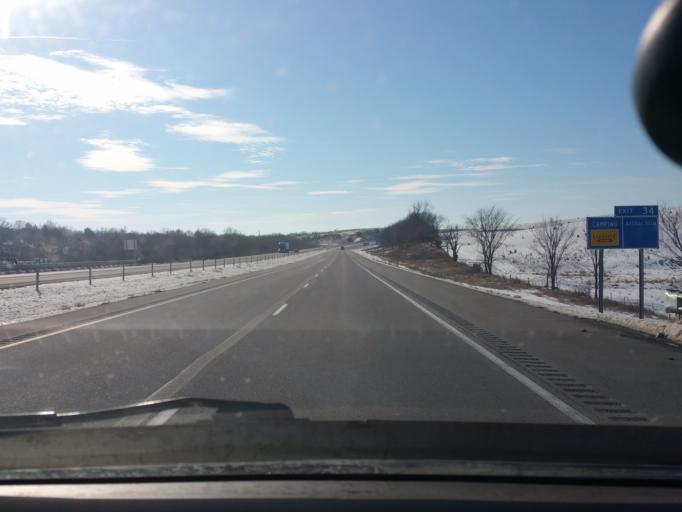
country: US
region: Iowa
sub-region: Clarke County
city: Osceola
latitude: 41.0591
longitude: -93.7818
